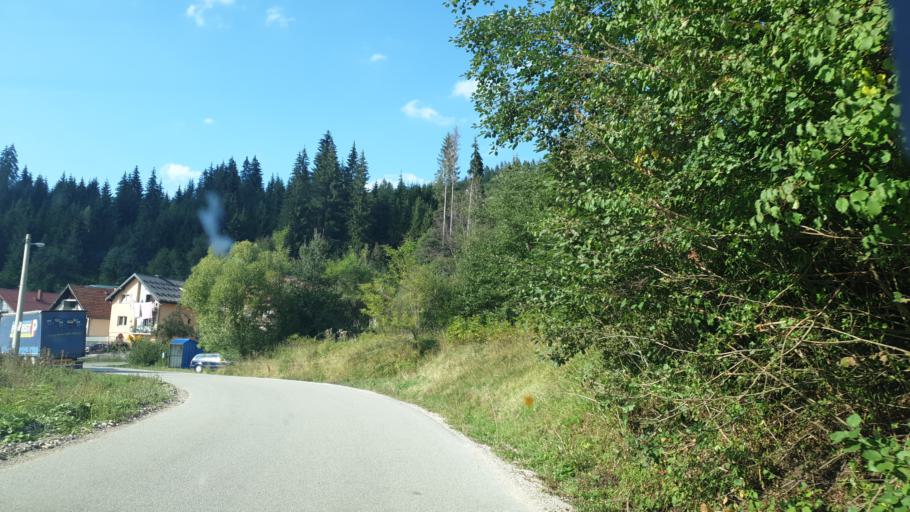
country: RS
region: Central Serbia
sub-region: Zlatiborski Okrug
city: Nova Varos
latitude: 43.4490
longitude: 19.8489
